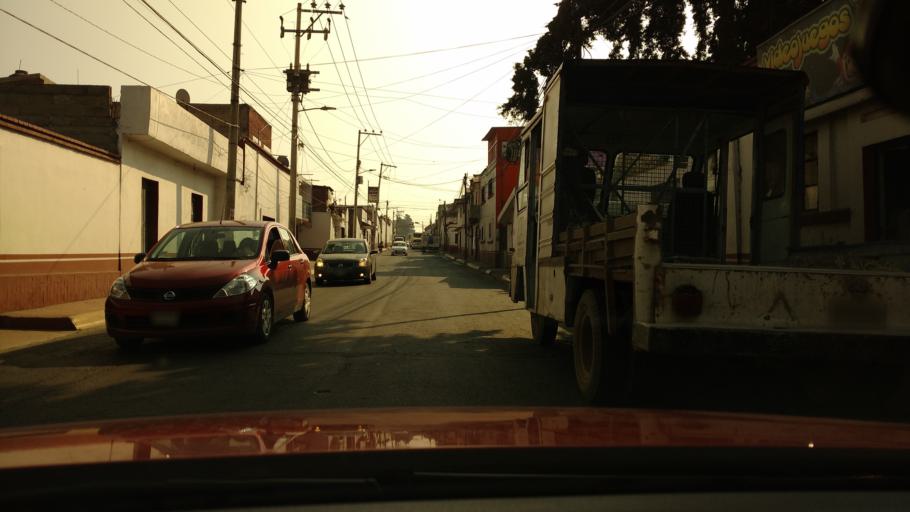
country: MX
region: Morelos
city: Chapultepec
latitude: 19.2033
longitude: -99.5632
